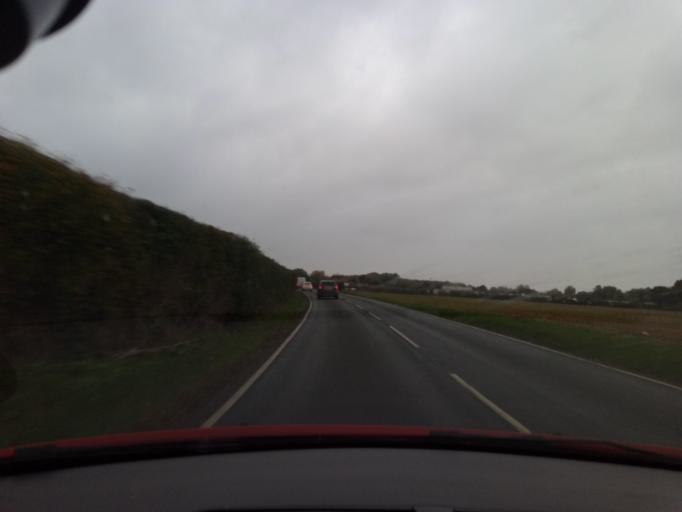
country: GB
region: England
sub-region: Suffolk
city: Kedington
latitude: 52.0553
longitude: 0.4973
